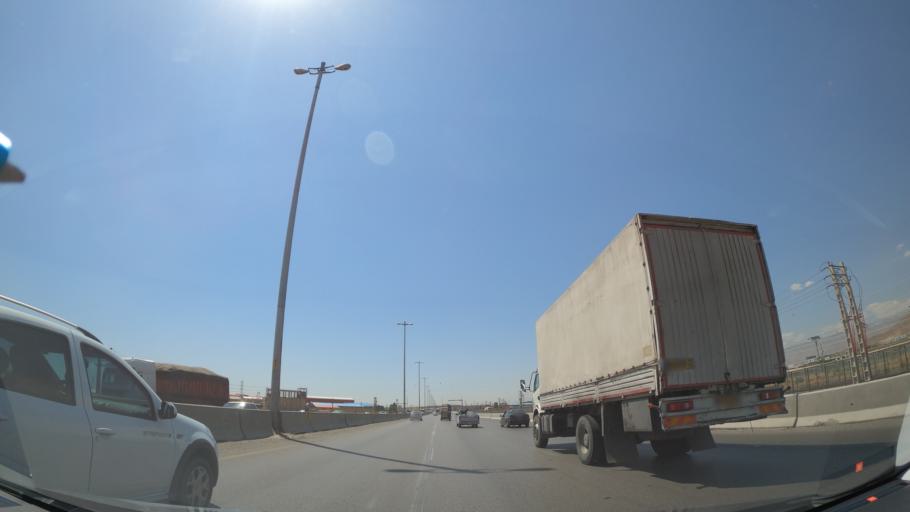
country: IR
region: Alborz
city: Karaj
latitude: 35.9057
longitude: 50.8459
